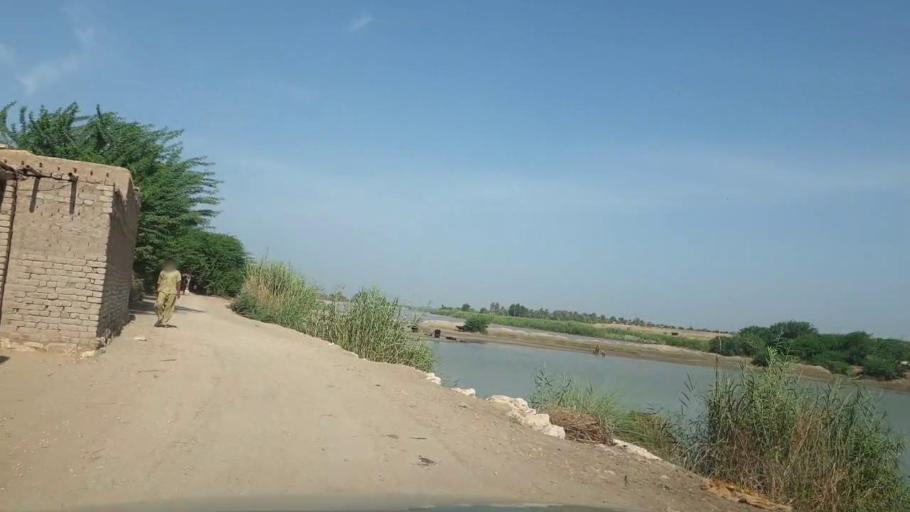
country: PK
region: Sindh
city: Rohri
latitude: 27.6295
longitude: 68.9048
